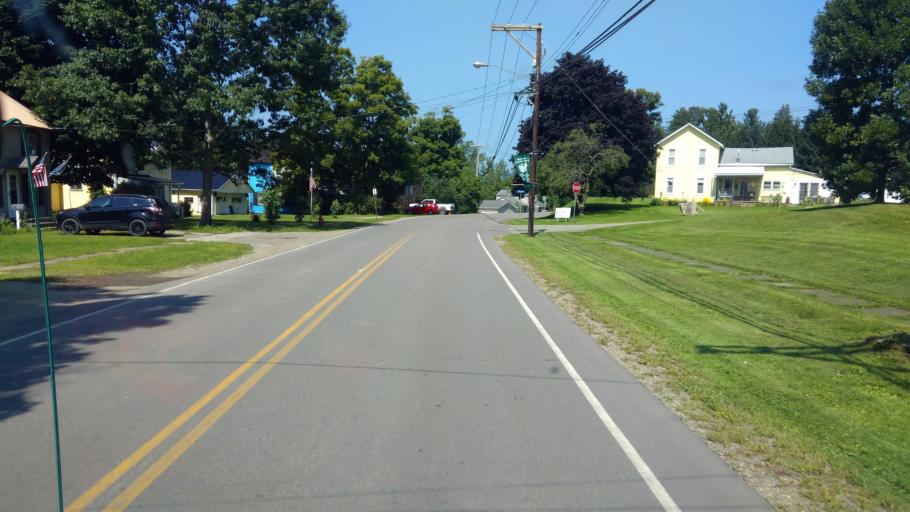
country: US
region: New York
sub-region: Allegany County
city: Belmont
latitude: 42.2292
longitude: -78.0349
